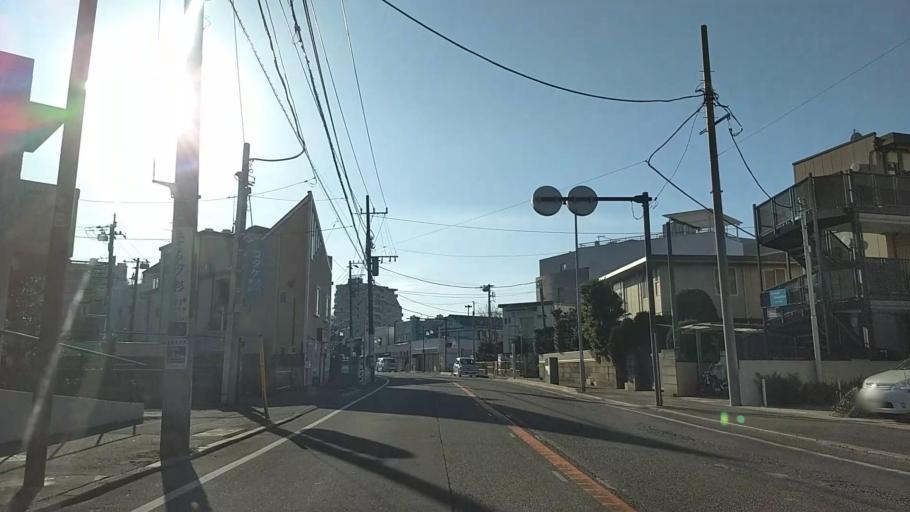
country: JP
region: Kanagawa
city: Fujisawa
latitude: 35.3127
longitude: 139.4864
